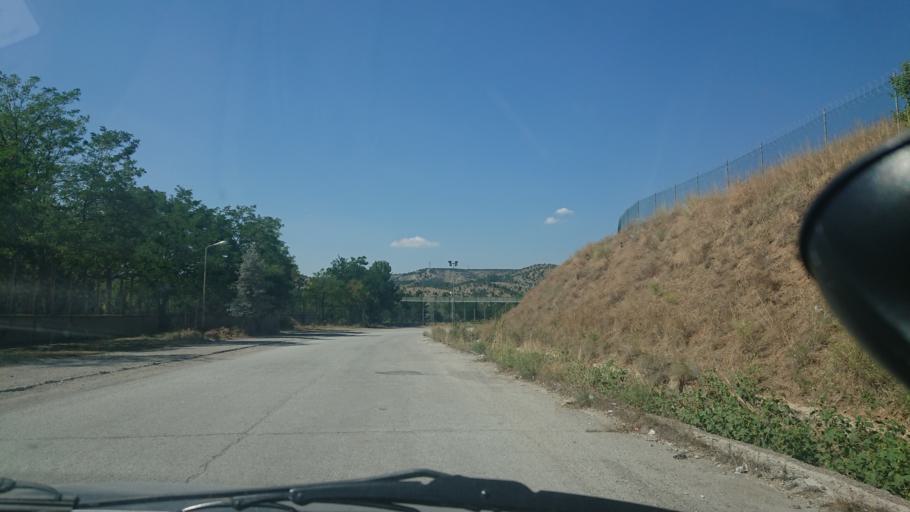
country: TR
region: Ankara
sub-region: Goelbasi
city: Golbasi
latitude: 39.8093
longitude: 32.8211
